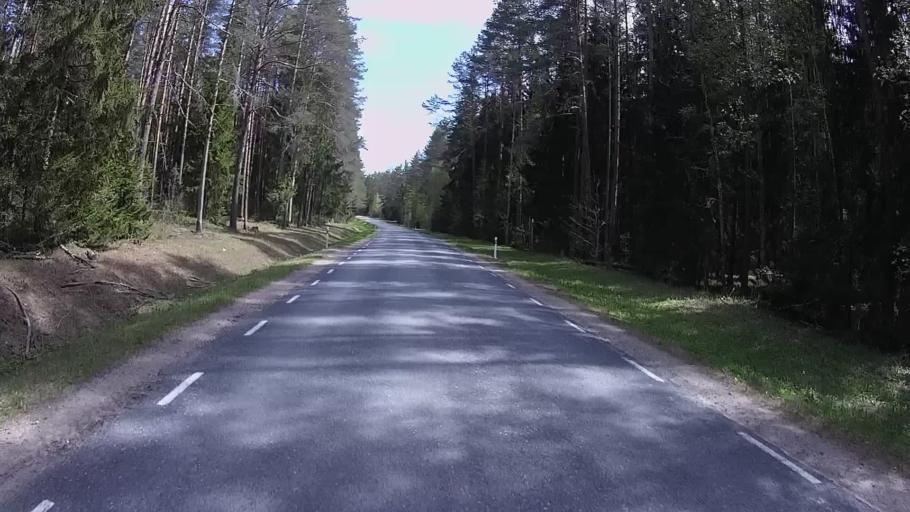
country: LV
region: Apes Novads
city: Ape
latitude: 57.6039
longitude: 26.4820
